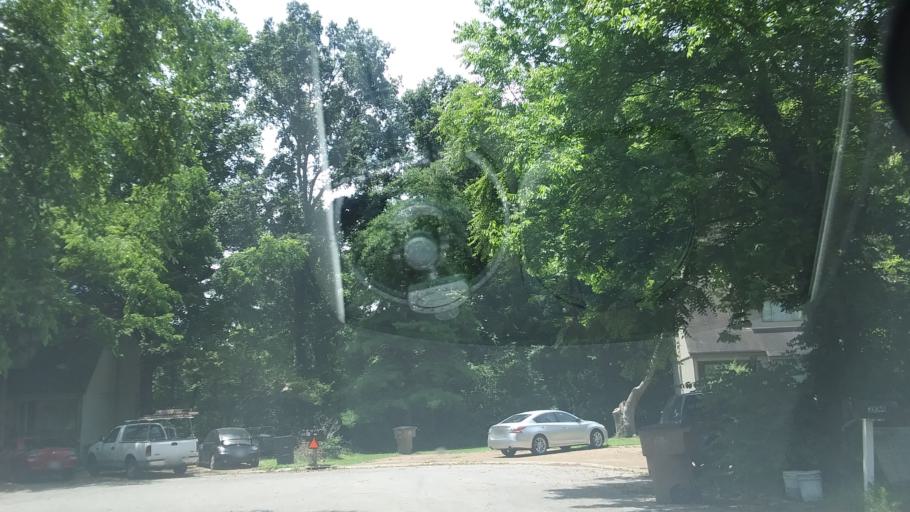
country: US
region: Tennessee
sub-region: Rutherford County
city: La Vergne
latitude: 36.0914
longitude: -86.6425
